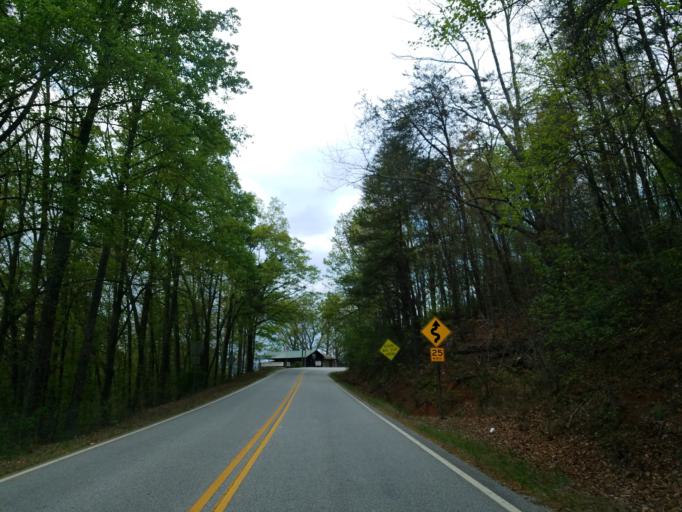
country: US
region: Georgia
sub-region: Lumpkin County
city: Dahlonega
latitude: 34.6083
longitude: -83.9702
